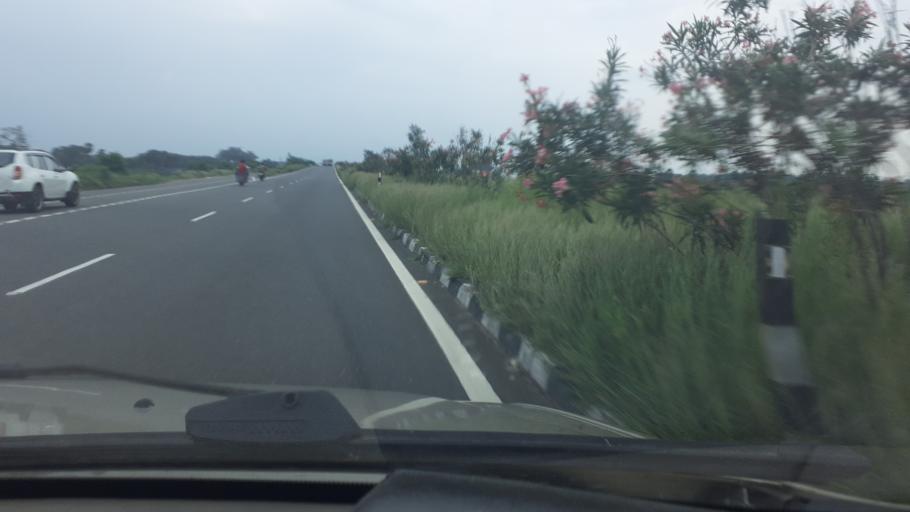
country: IN
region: Tamil Nadu
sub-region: Madurai
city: Tirupparangunram
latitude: 9.8169
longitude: 77.9791
